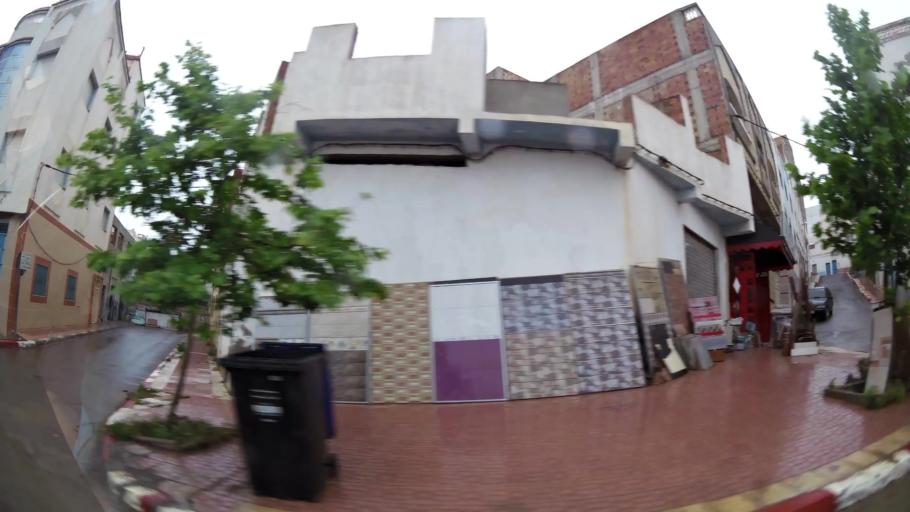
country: MA
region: Taza-Al Hoceima-Taounate
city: Imzourene
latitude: 35.1539
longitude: -3.8489
